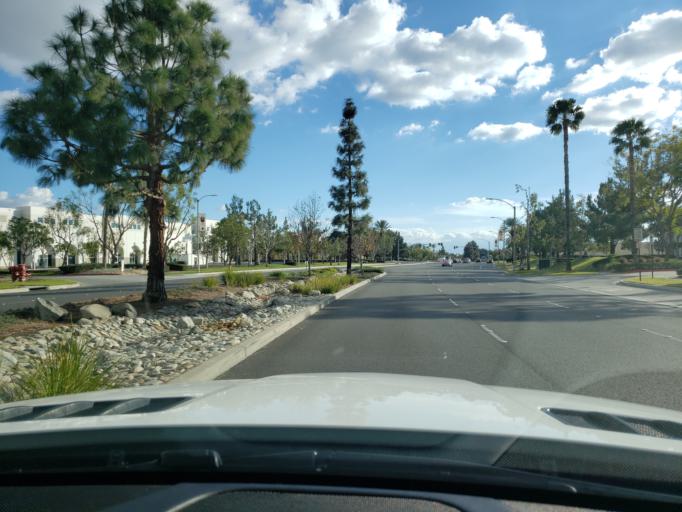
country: US
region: California
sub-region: San Bernardino County
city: Rancho Cucamonga
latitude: 34.1011
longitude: -117.5560
